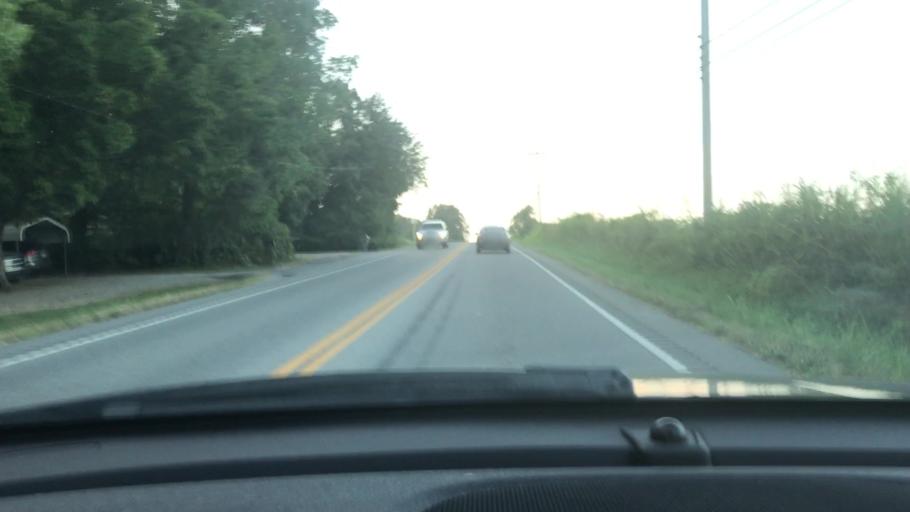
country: US
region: Tennessee
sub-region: Dickson County
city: Dickson
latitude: 36.0918
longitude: -87.3765
